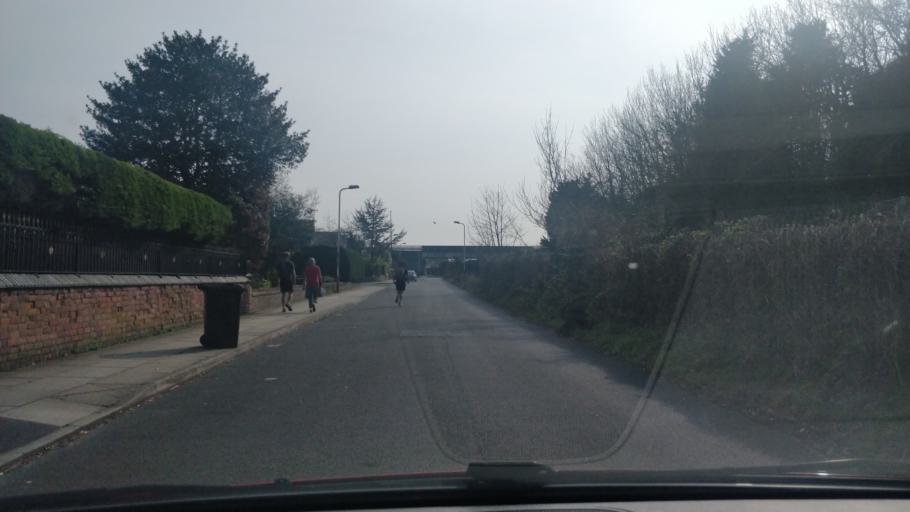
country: GB
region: England
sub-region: Sefton
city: Formby
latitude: 53.6003
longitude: -3.0438
